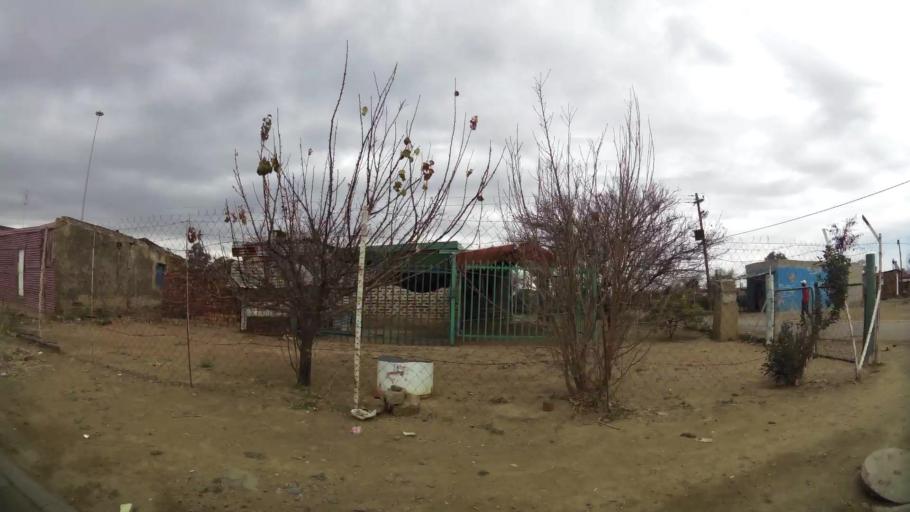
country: ZA
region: Orange Free State
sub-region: Fezile Dabi District Municipality
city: Kroonstad
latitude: -27.6479
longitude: 27.2152
